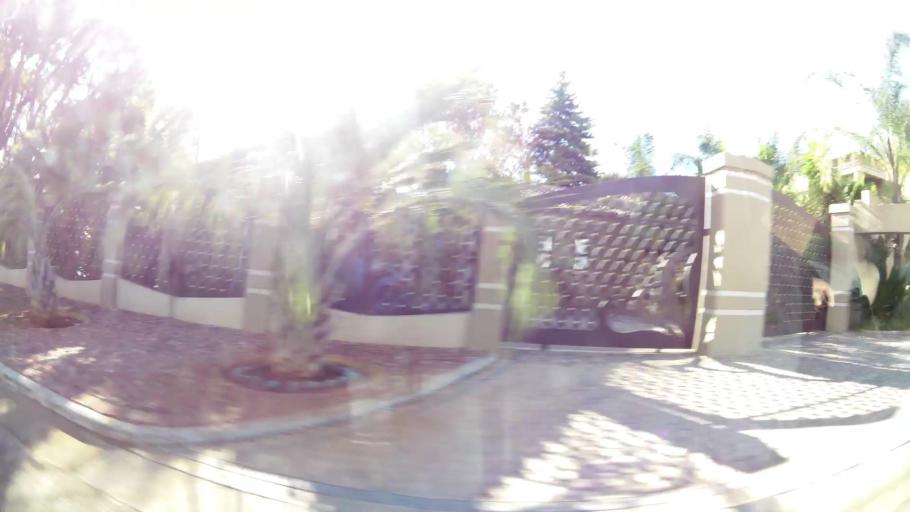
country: ZA
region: North-West
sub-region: Dr Kenneth Kaunda District Municipality
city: Klerksdorp
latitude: -26.8280
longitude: 26.6711
